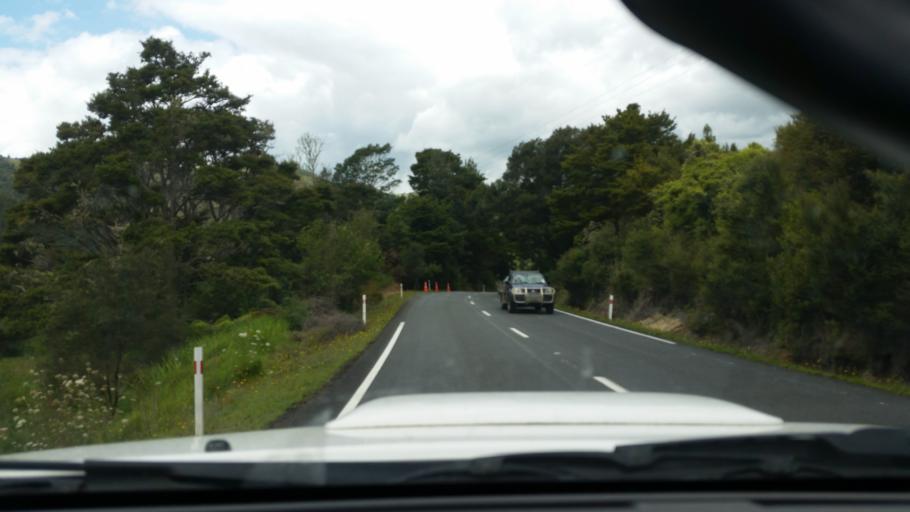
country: NZ
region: Northland
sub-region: Kaipara District
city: Dargaville
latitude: -35.7879
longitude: 173.9106
